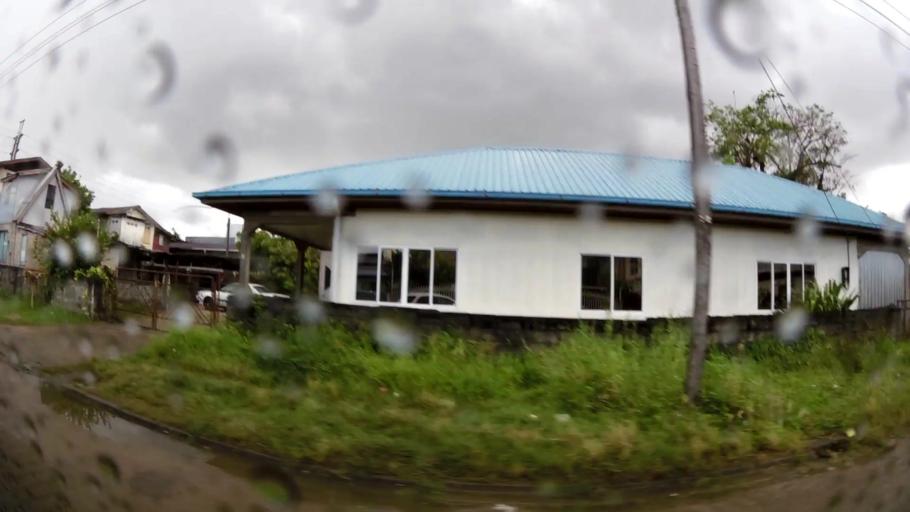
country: SR
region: Paramaribo
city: Paramaribo
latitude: 5.8177
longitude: -55.1750
